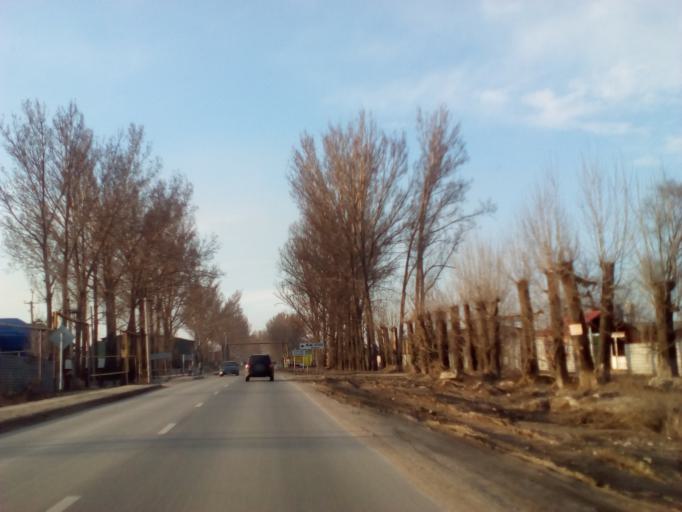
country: KZ
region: Almaty Oblysy
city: Burunday
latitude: 43.2470
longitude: 76.7854
